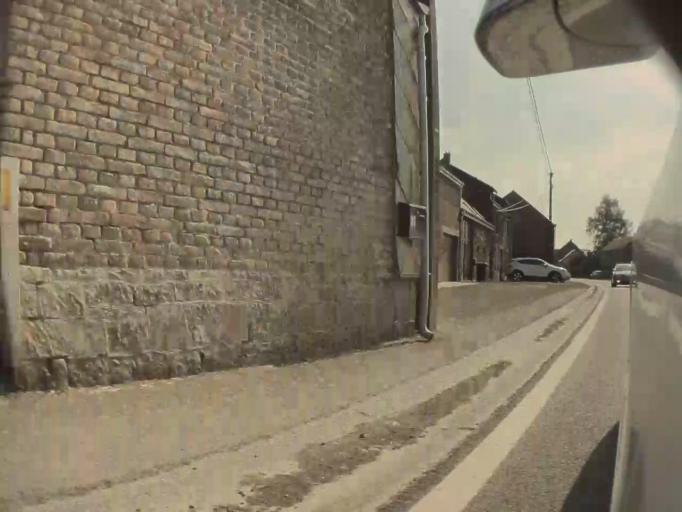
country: BE
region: Wallonia
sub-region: Province de Namur
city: Somme-Leuze
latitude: 50.3528
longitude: 5.3086
